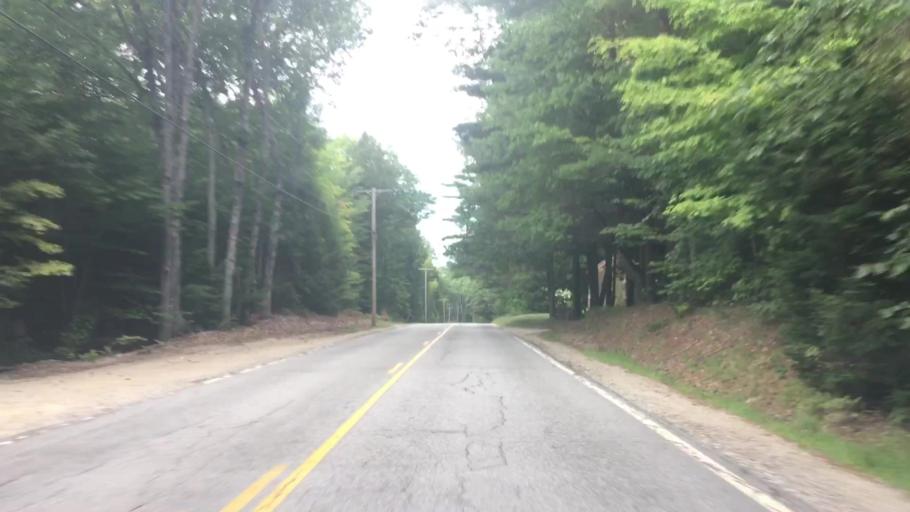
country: US
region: Maine
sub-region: Oxford County
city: Oxford
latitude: 44.0267
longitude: -70.5304
